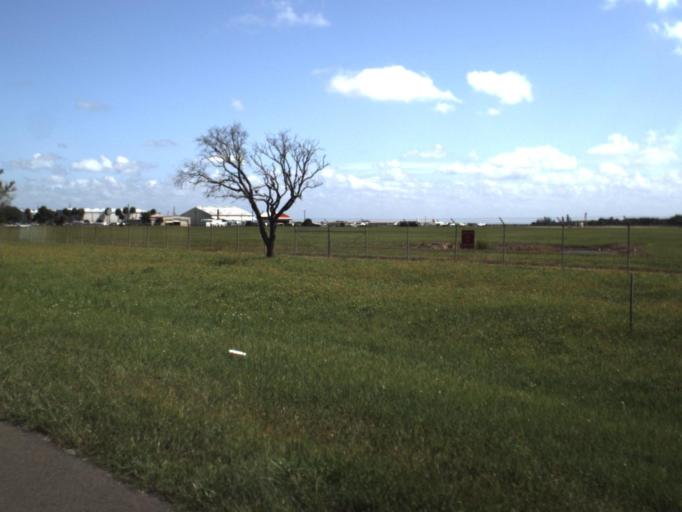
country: US
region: Florida
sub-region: Pinellas County
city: South Highpoint
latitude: 27.8985
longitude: -82.6929
